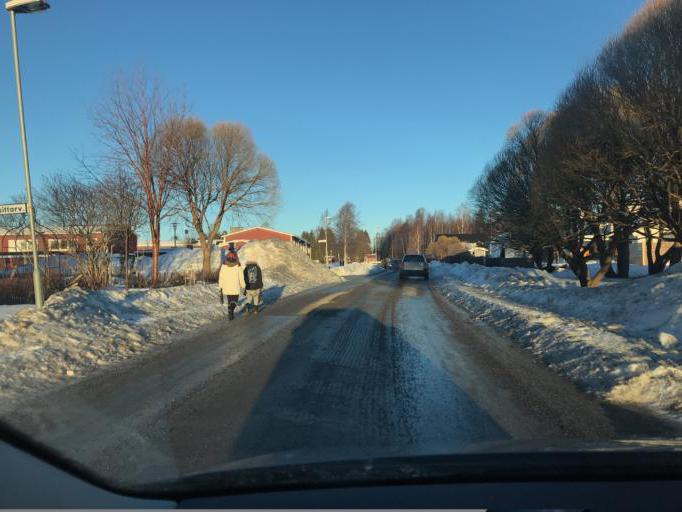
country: SE
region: Norrbotten
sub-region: Lulea Kommun
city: Sodra Sunderbyn
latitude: 65.6566
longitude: 21.9527
